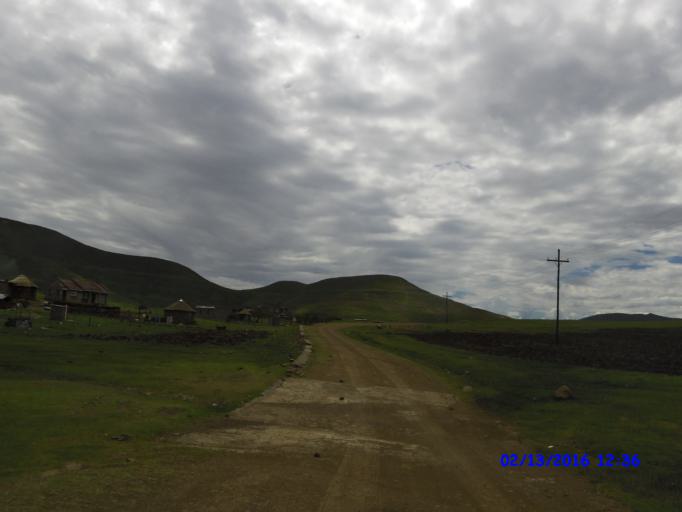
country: LS
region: Maseru
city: Nako
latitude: -29.8385
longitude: 28.0248
